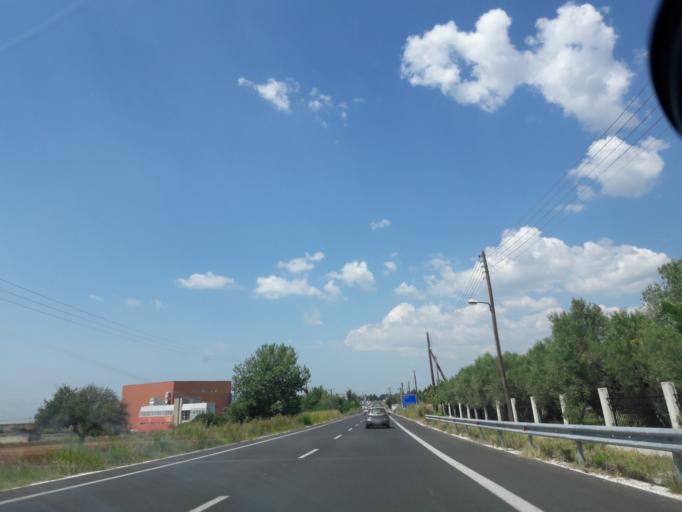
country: GR
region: Central Macedonia
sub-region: Nomos Thessalonikis
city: Agia Paraskevi
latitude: 40.5153
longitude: 23.0706
